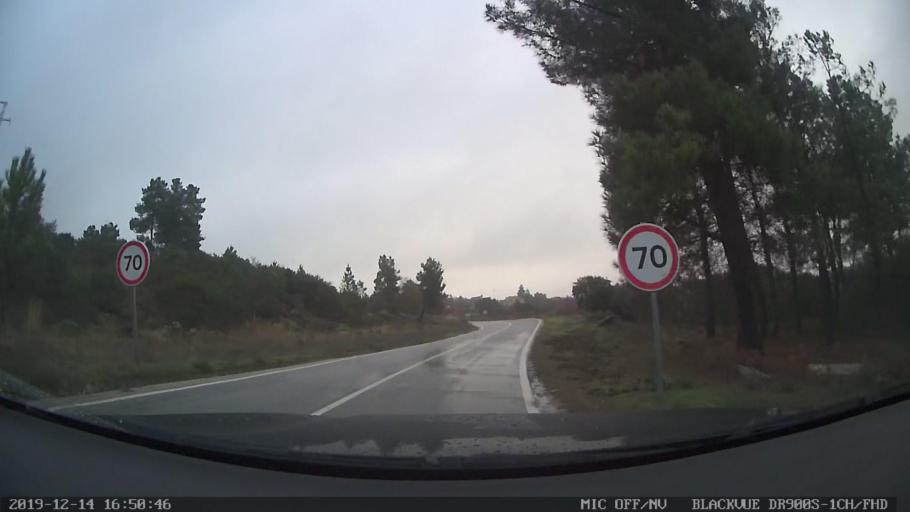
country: PT
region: Vila Real
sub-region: Murca
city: Murca
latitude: 41.4189
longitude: -7.5066
